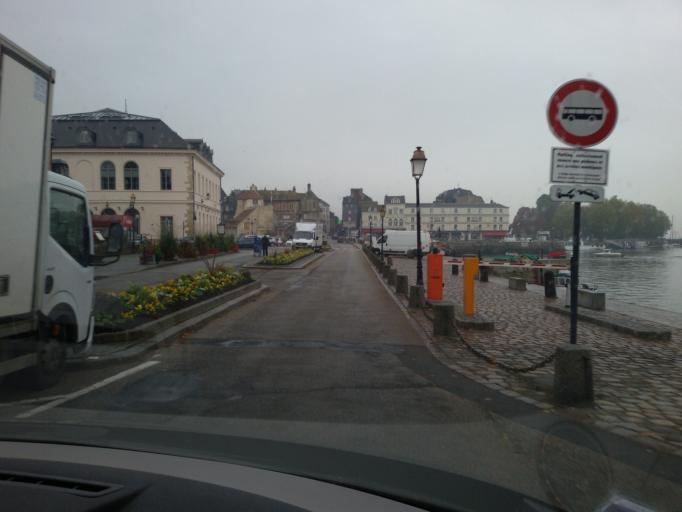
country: FR
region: Lower Normandy
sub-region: Departement du Calvados
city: Honfleur
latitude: 49.4199
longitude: 0.2356
